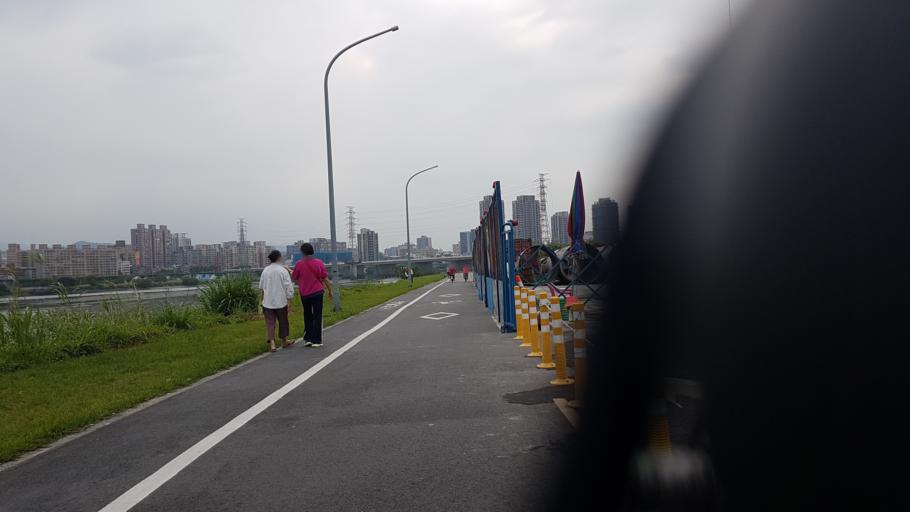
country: TW
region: Taipei
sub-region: Taipei
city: Banqiao
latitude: 25.0144
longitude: 121.5000
